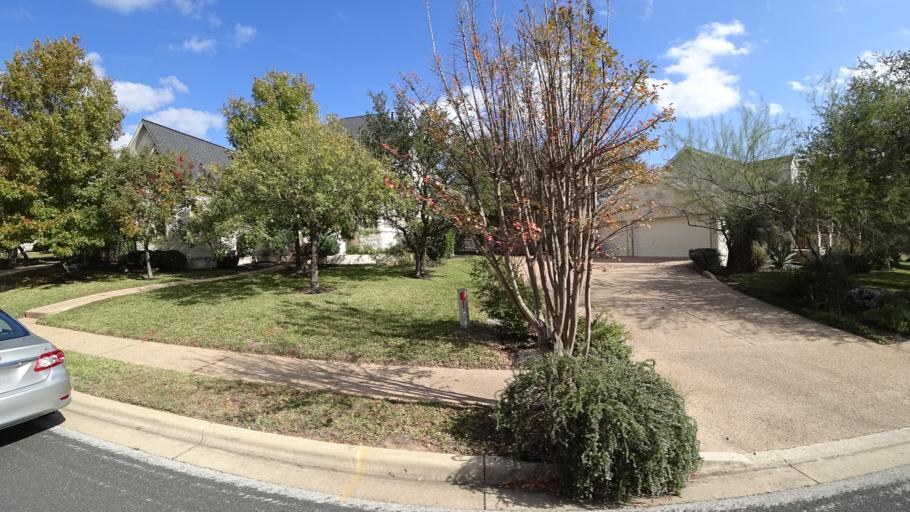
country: US
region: Texas
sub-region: Williamson County
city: Anderson Mill
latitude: 30.4254
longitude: -97.8111
